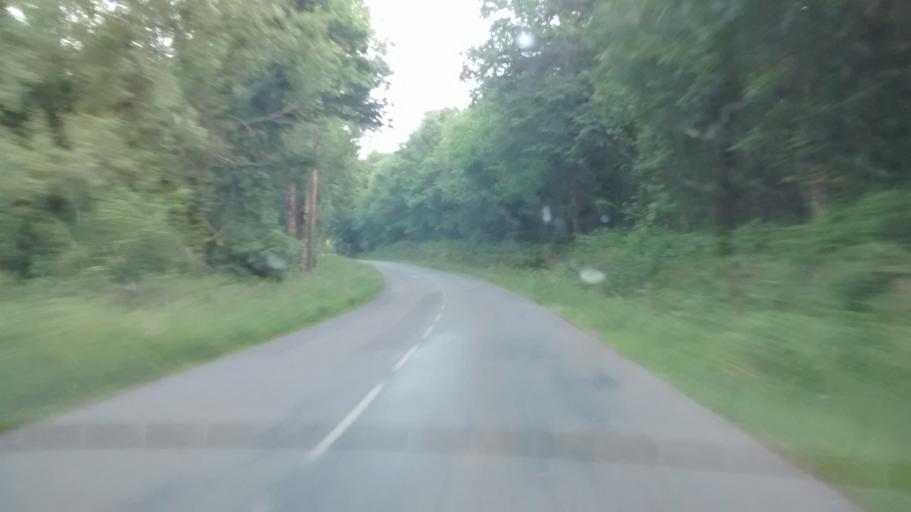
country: FR
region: Brittany
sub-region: Departement du Morbihan
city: Beignon
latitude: 47.9893
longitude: -2.1444
